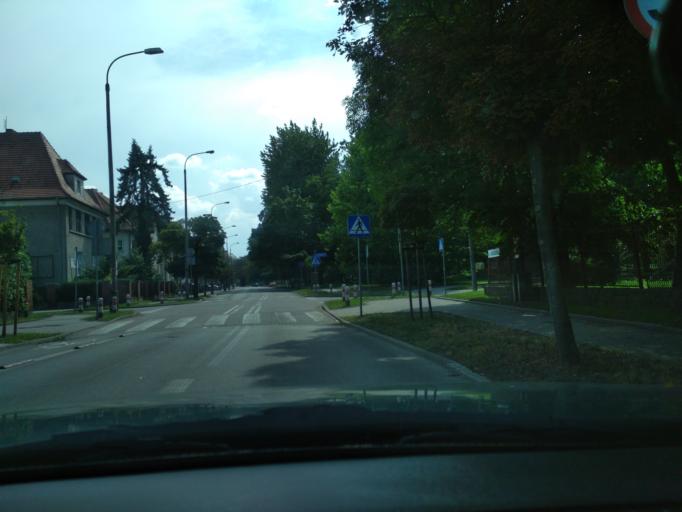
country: PL
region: Silesian Voivodeship
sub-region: Powiat raciborski
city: Raciborz
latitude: 50.0860
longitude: 18.2108
